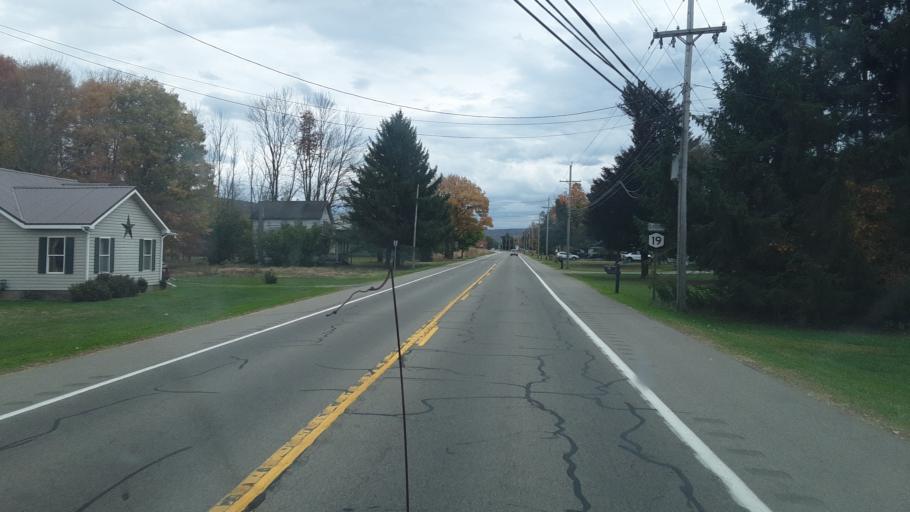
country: US
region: New York
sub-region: Allegany County
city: Belmont
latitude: 42.2085
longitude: -78.0136
